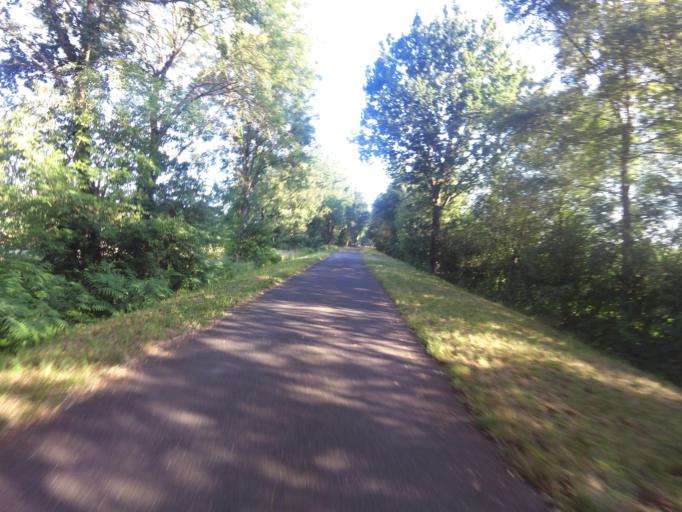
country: FR
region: Brittany
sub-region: Departement du Morbihan
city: Malestroit
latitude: 47.8457
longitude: -2.4388
